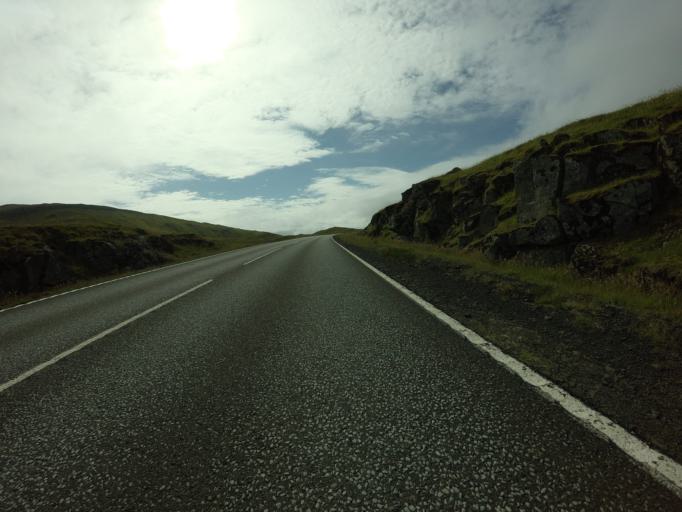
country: FO
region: Sandoy
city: Sandur
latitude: 61.8931
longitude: -6.8650
